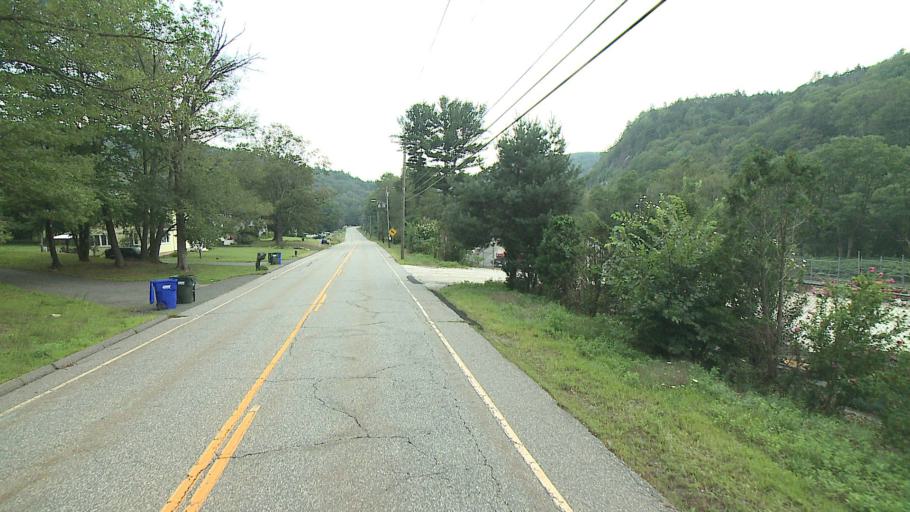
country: US
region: Connecticut
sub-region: Litchfield County
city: Thomaston
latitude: 41.6385
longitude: -73.0779
